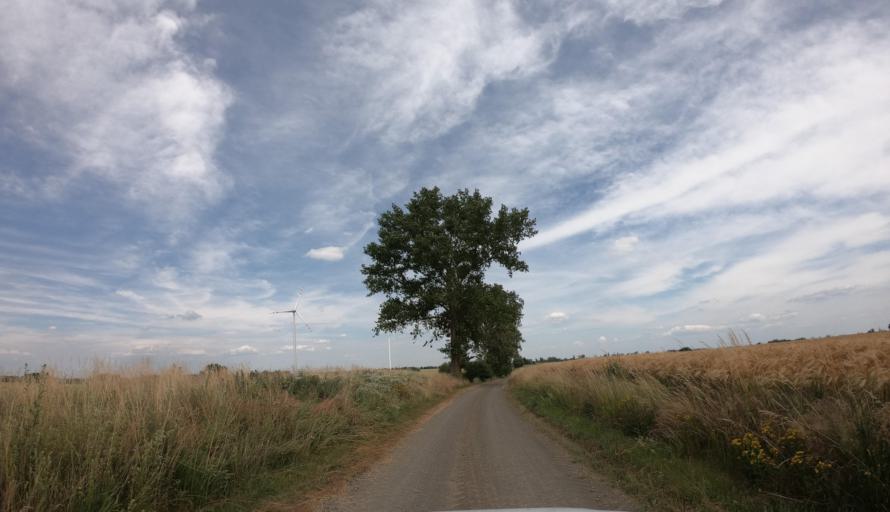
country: PL
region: West Pomeranian Voivodeship
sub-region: Powiat pyrzycki
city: Kozielice
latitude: 53.1174
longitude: 14.8285
